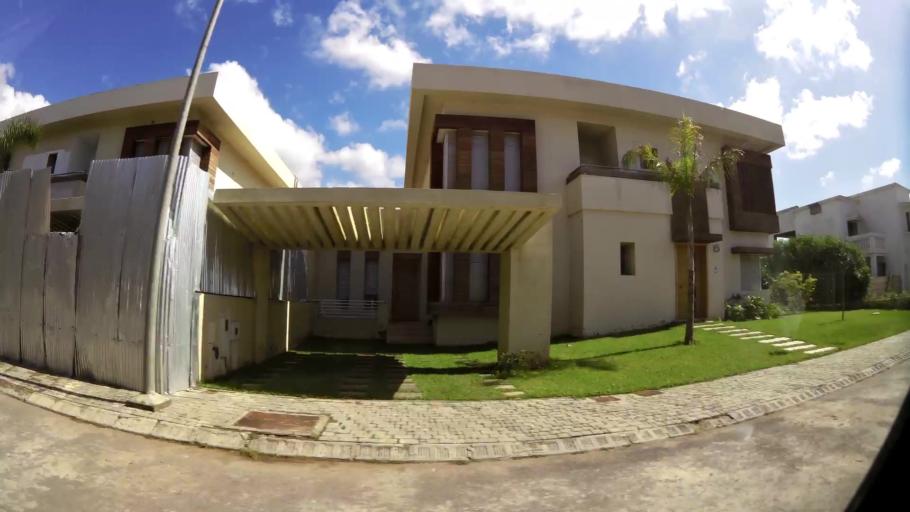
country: MA
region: Grand Casablanca
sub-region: Nouaceur
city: Bouskoura
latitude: 33.4643
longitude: -7.5989
